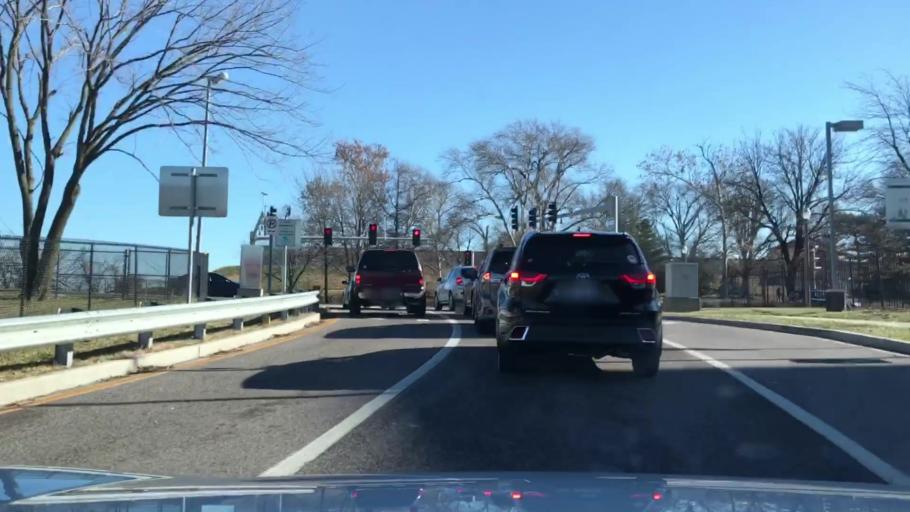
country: US
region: Missouri
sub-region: City of Saint Louis
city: St. Louis
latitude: 38.6163
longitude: -90.2400
